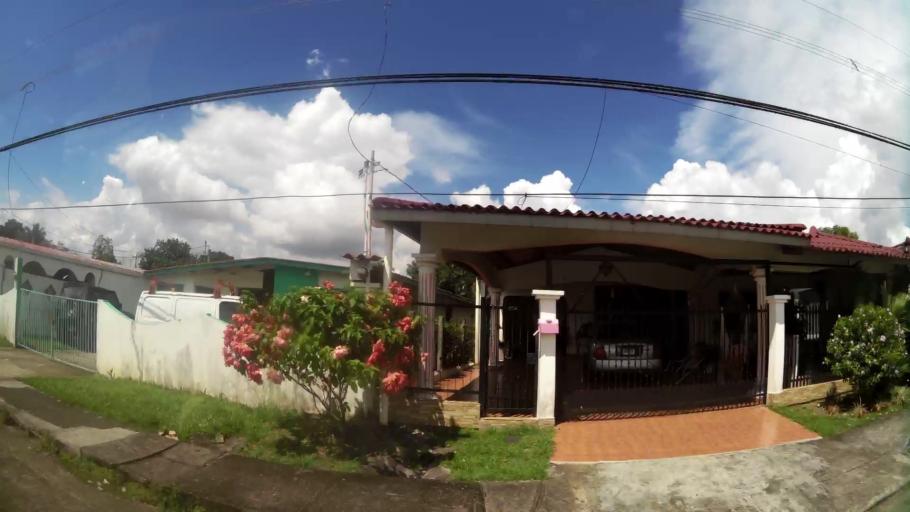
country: PA
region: Panama
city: Vista Alegre
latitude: 8.9229
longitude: -79.6944
